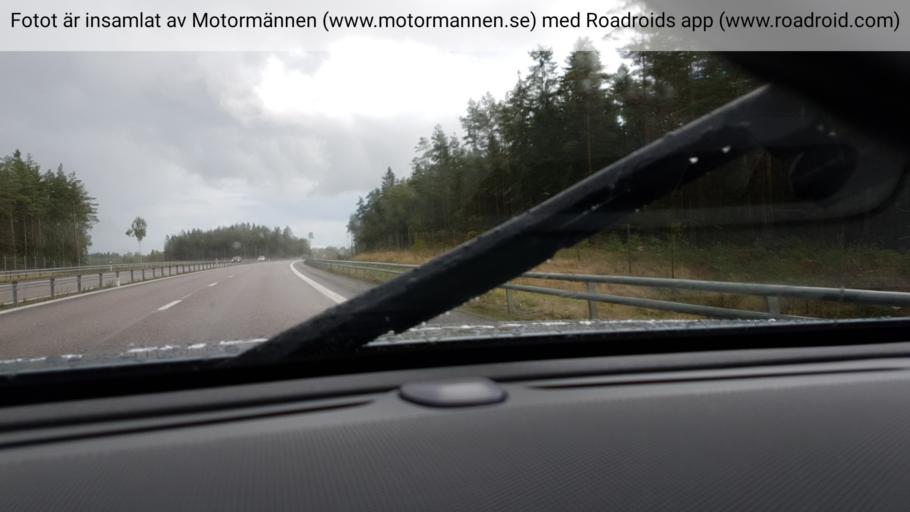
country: SE
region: Vaestra Goetaland
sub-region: Trollhattan
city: Sjuntorp
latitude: 58.2279
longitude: 12.2183
